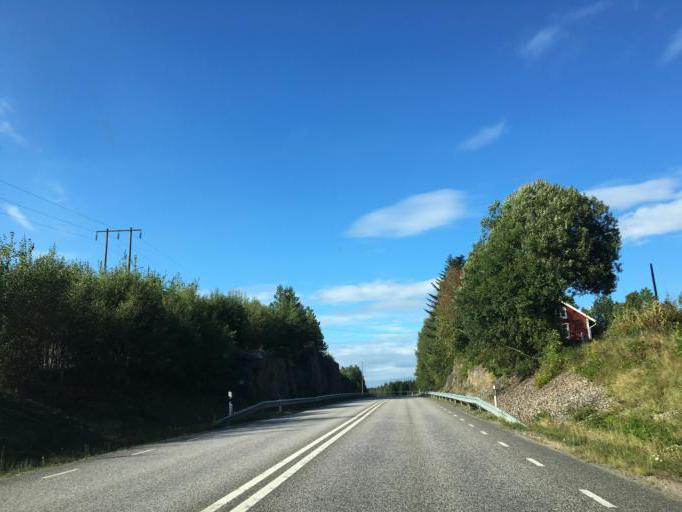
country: SE
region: Soedermanland
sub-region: Nykopings Kommun
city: Nykoping
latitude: 58.8250
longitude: 16.9299
